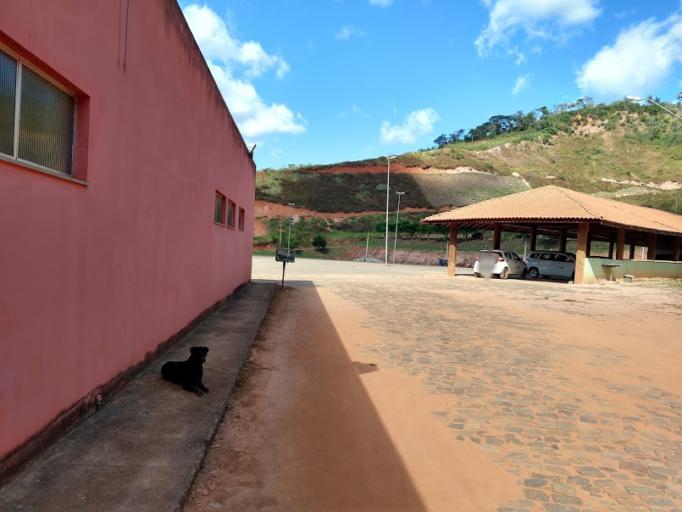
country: BR
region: Minas Gerais
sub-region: Vicosa
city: Vicosa
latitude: -20.6890
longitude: -42.6066
